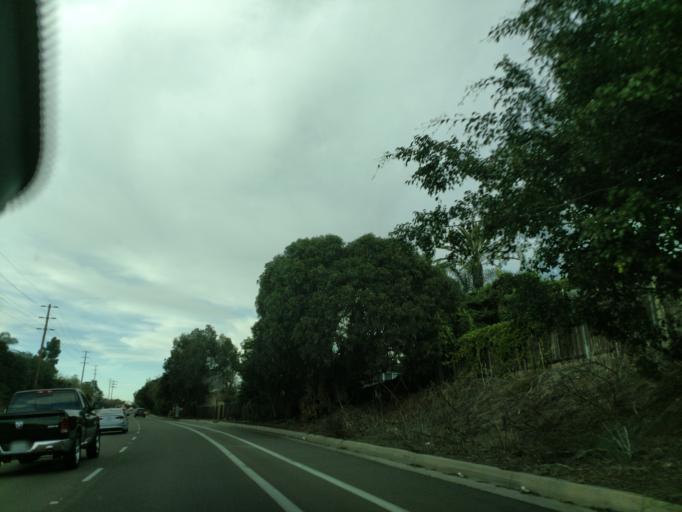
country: US
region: California
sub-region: San Diego County
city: Coronado
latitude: 32.7334
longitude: -117.2286
